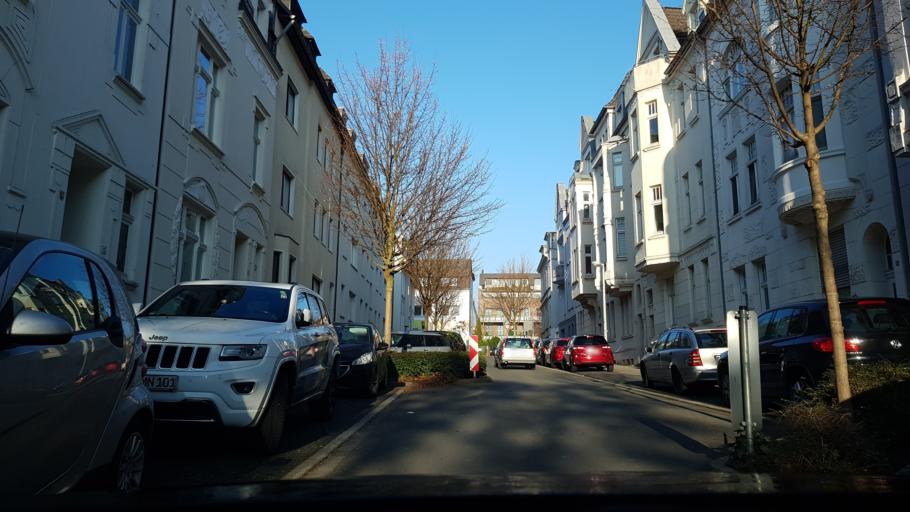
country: DE
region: North Rhine-Westphalia
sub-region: Regierungsbezirk Dusseldorf
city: Muelheim (Ruhr)
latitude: 51.4301
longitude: 6.8951
